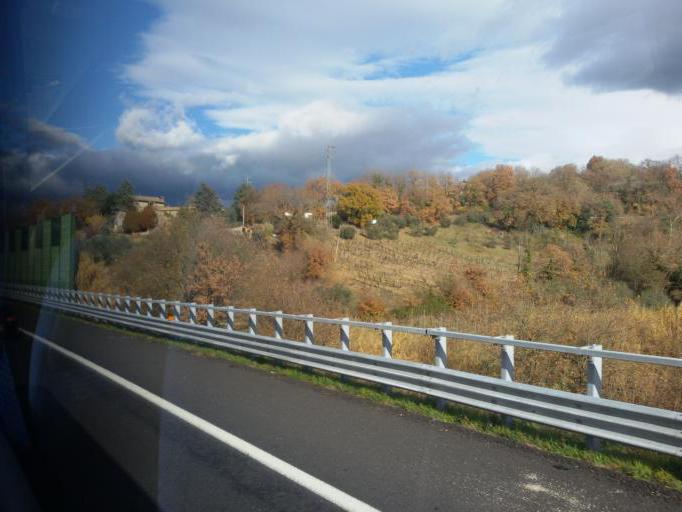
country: IT
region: Umbria
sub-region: Provincia di Terni
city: Baschi
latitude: 42.6832
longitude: 12.2115
